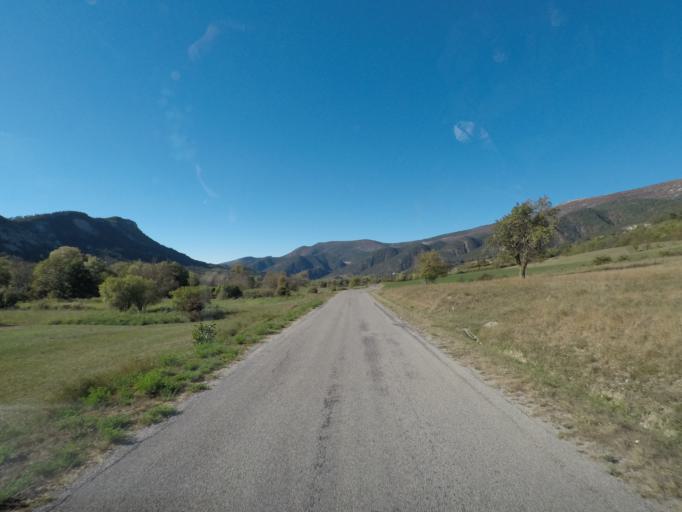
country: FR
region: Provence-Alpes-Cote d'Azur
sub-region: Departement des Hautes-Alpes
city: Serres
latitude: 44.4525
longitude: 5.5351
